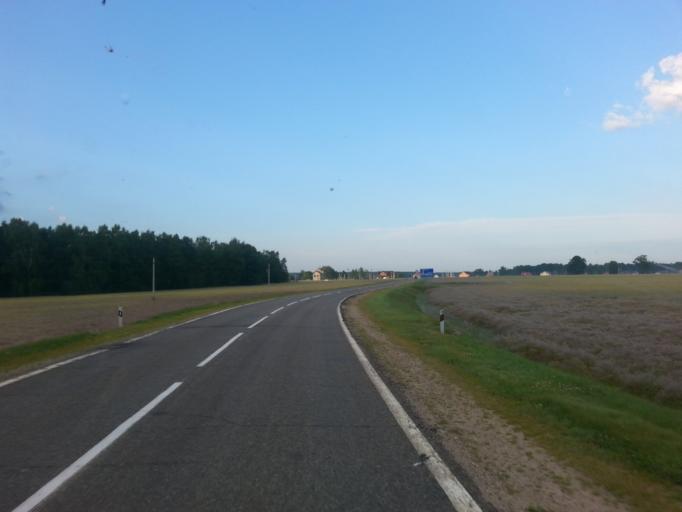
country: BY
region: Minsk
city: Il'ya
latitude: 54.5154
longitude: 27.2240
